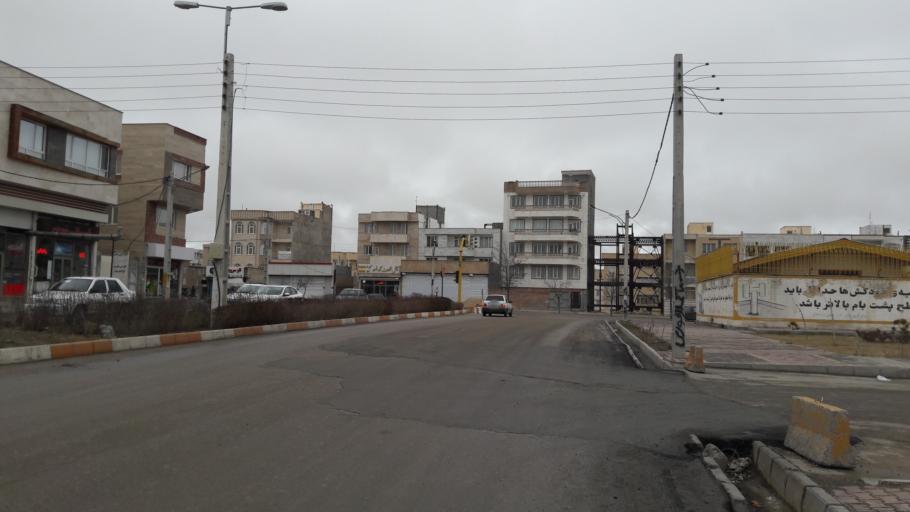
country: IR
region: Ardabil
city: Ardabil
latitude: 38.2180
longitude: 48.3075
